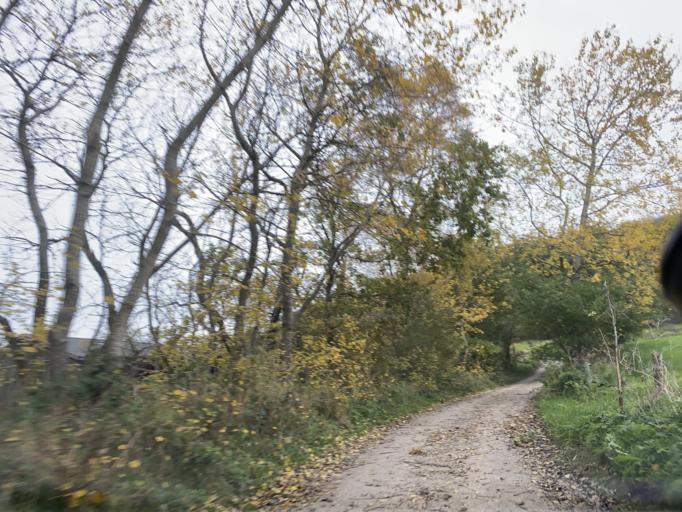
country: DK
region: Central Jutland
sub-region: Favrskov Kommune
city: Hammel
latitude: 56.1970
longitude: 9.7811
